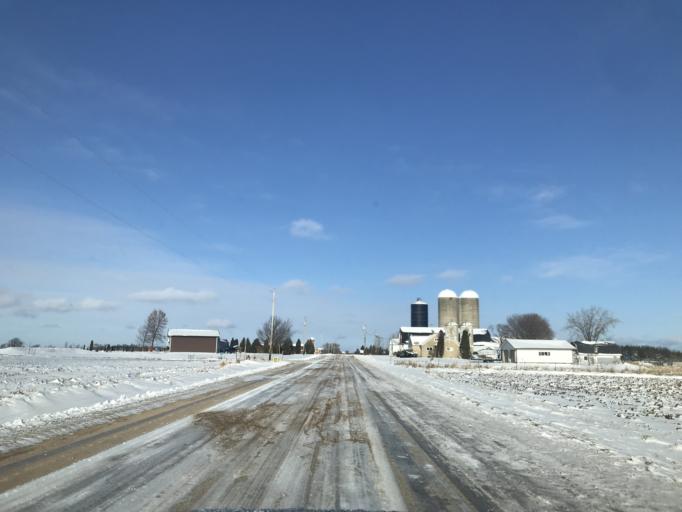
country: US
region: Wisconsin
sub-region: Kewaunee County
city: Algoma
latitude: 44.7004
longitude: -87.6004
